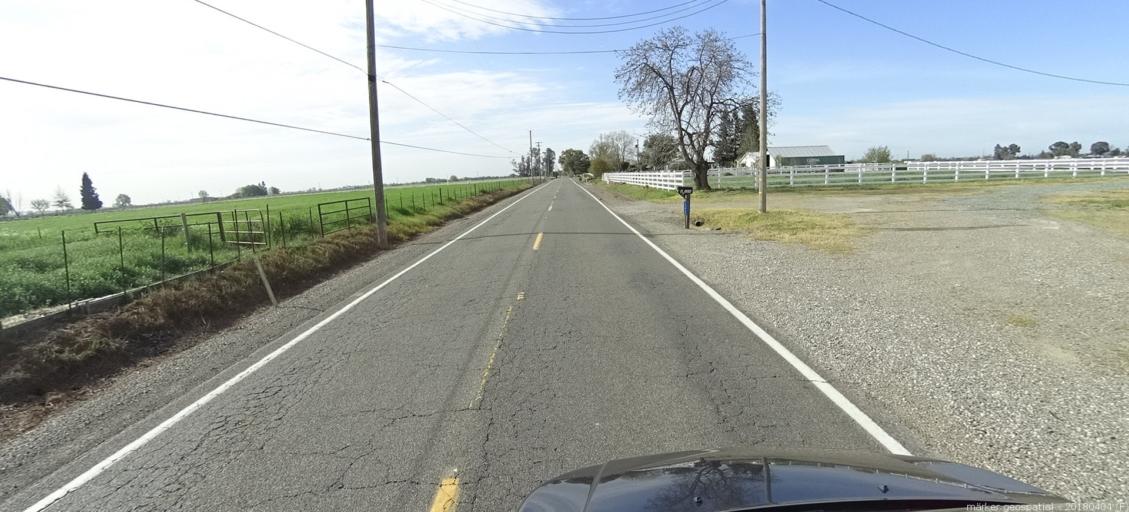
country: US
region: California
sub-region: Sacramento County
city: Herald
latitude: 38.2689
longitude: -121.2266
